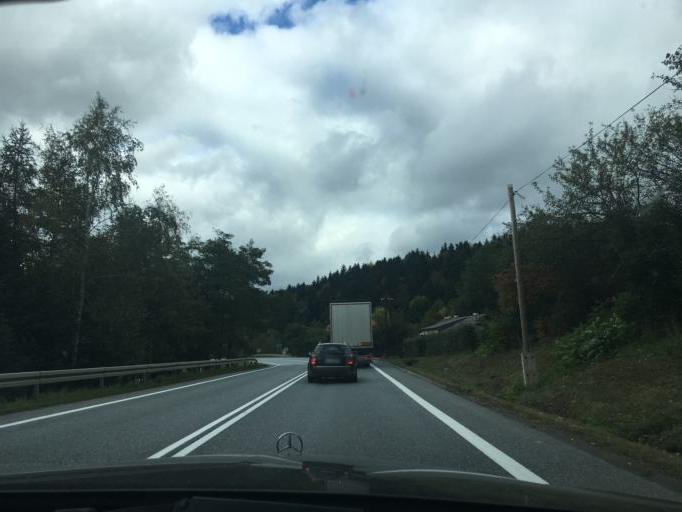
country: PL
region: Subcarpathian Voivodeship
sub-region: Powiat krosnienski
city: Dukla
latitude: 49.5738
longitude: 21.7005
